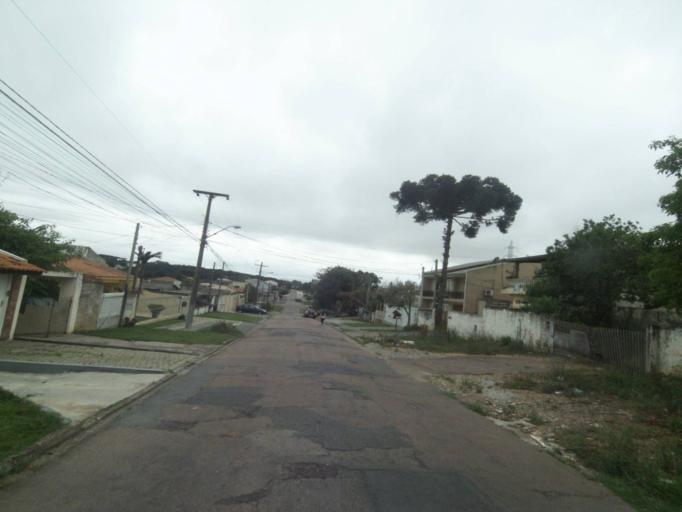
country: BR
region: Parana
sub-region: Sao Jose Dos Pinhais
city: Sao Jose dos Pinhais
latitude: -25.5428
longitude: -49.2852
